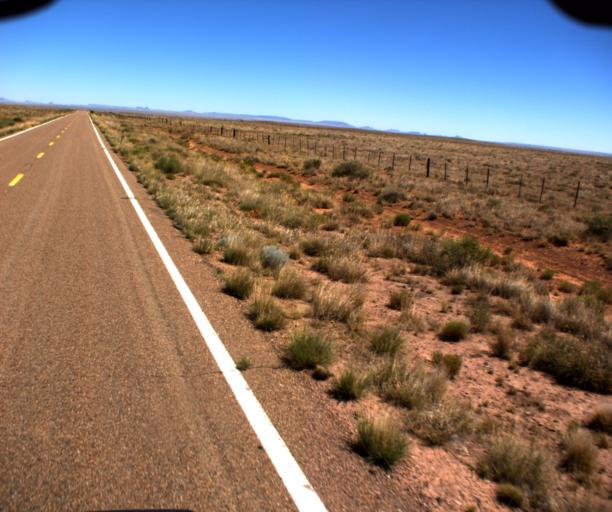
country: US
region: Arizona
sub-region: Navajo County
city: Winslow
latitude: 34.8864
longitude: -110.6497
